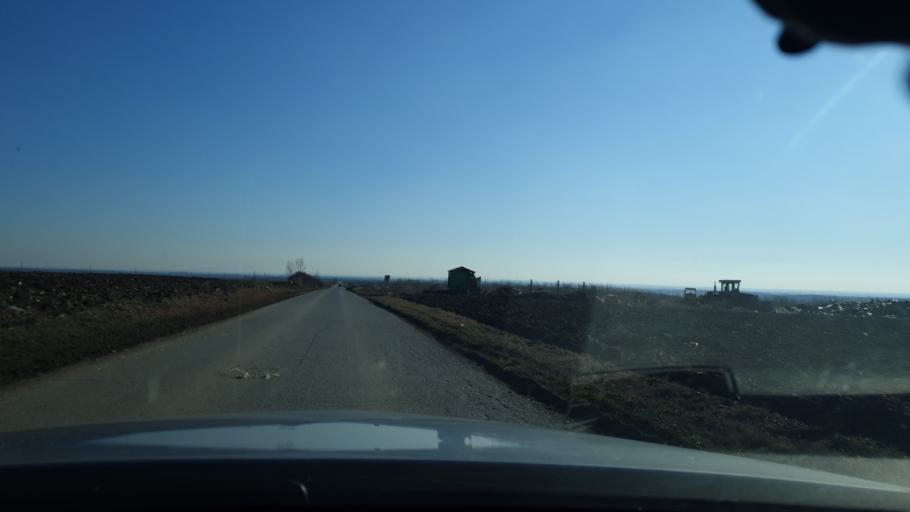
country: RS
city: Vrdnik
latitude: 45.0890
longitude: 19.8063
